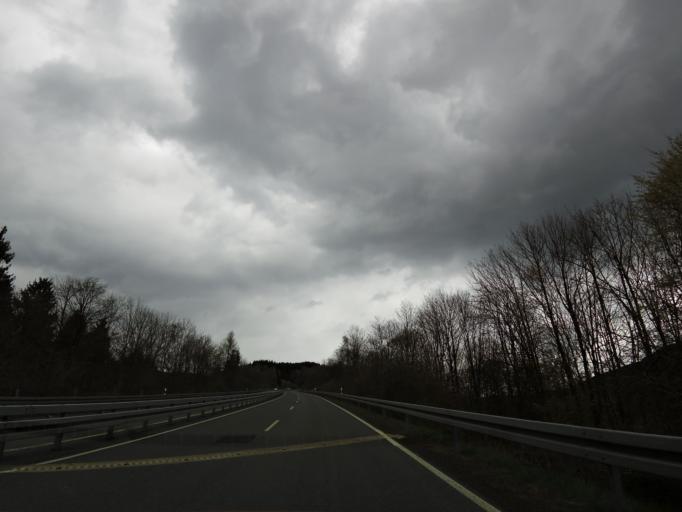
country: DE
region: Lower Saxony
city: Osterode am Harz
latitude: 51.7559
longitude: 10.2912
